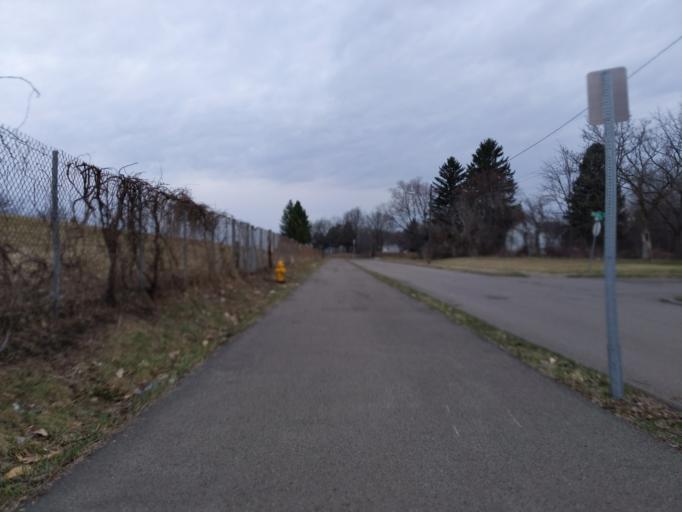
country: US
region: New York
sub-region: Chemung County
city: Elmira
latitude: 42.1092
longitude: -76.8126
